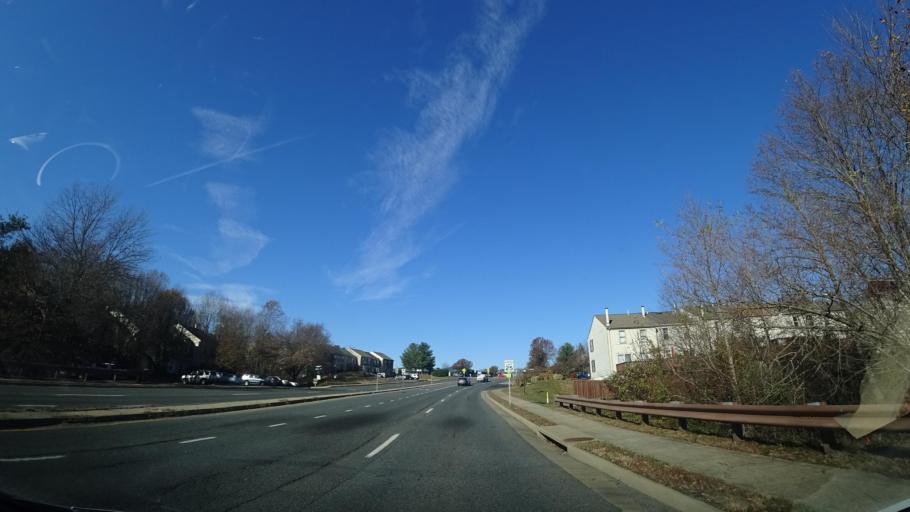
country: US
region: Virginia
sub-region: City of Fredericksburg
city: Fredericksburg
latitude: 38.2461
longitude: -77.5093
